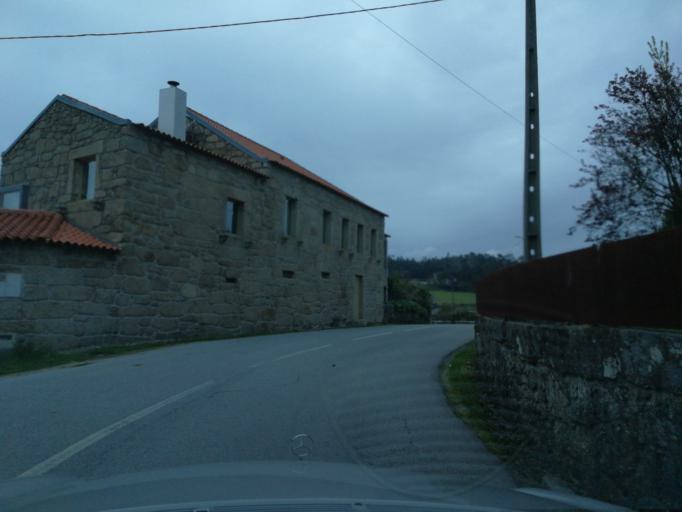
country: PT
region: Braga
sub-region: Braga
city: Oliveira
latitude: 41.4830
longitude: -8.4710
